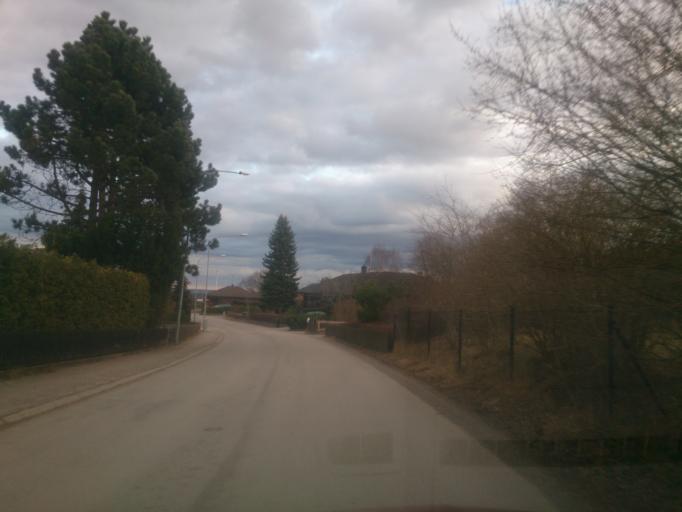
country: SE
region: OEstergoetland
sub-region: Norrkopings Kommun
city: Jursla
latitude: 58.6714
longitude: 16.1860
